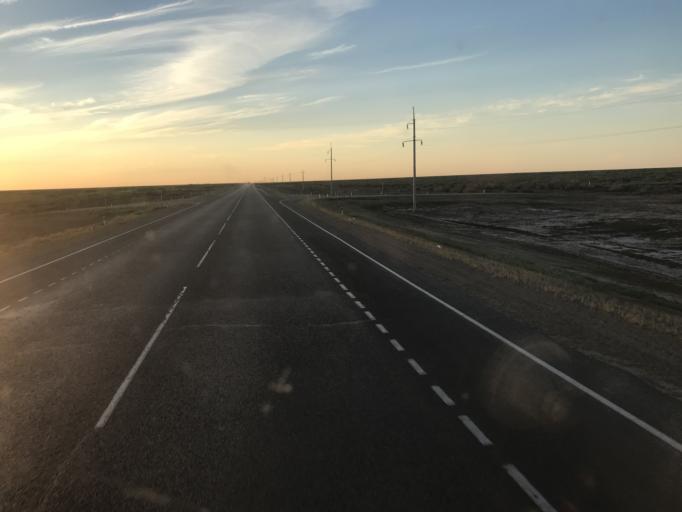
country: KZ
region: Qyzylorda
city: Zhosaly
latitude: 45.2445
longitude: 64.1188
